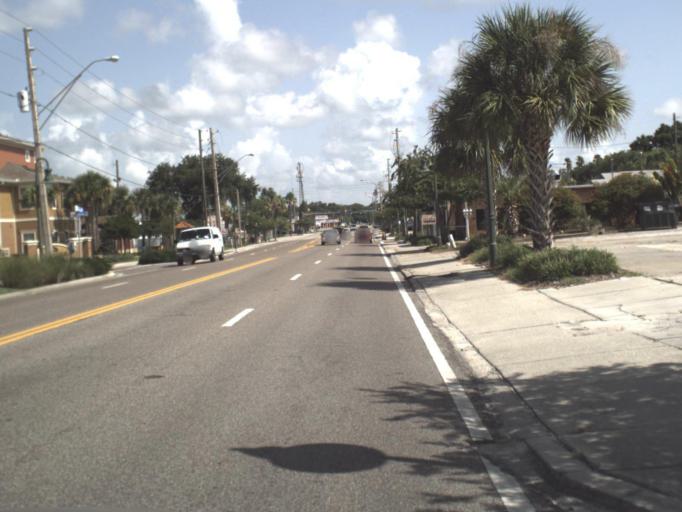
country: US
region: Florida
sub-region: Pinellas County
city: Belleair
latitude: 27.9323
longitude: -82.7956
